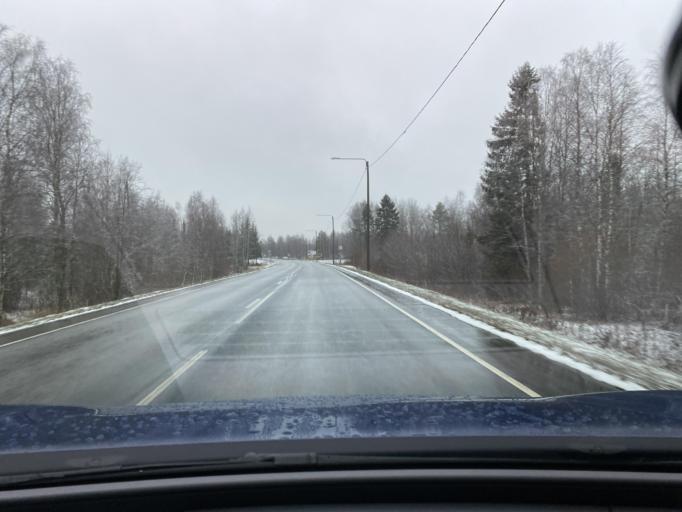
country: FI
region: Northern Ostrobothnia
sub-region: Oulu
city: Kiiminki
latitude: 65.1322
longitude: 25.8014
